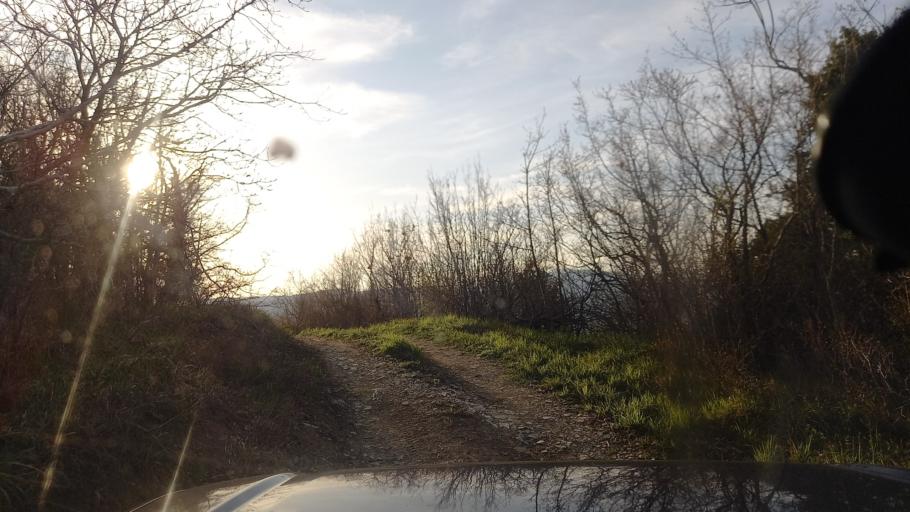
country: RU
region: Krasnodarskiy
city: Arkhipo-Osipovka
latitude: 44.3604
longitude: 38.5544
